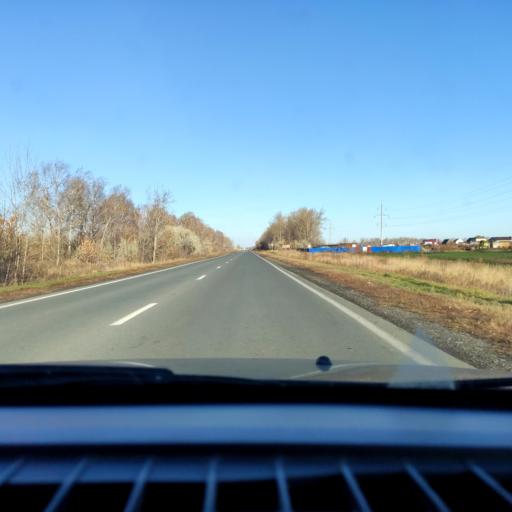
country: RU
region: Samara
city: Tol'yatti
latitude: 53.6226
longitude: 49.3083
